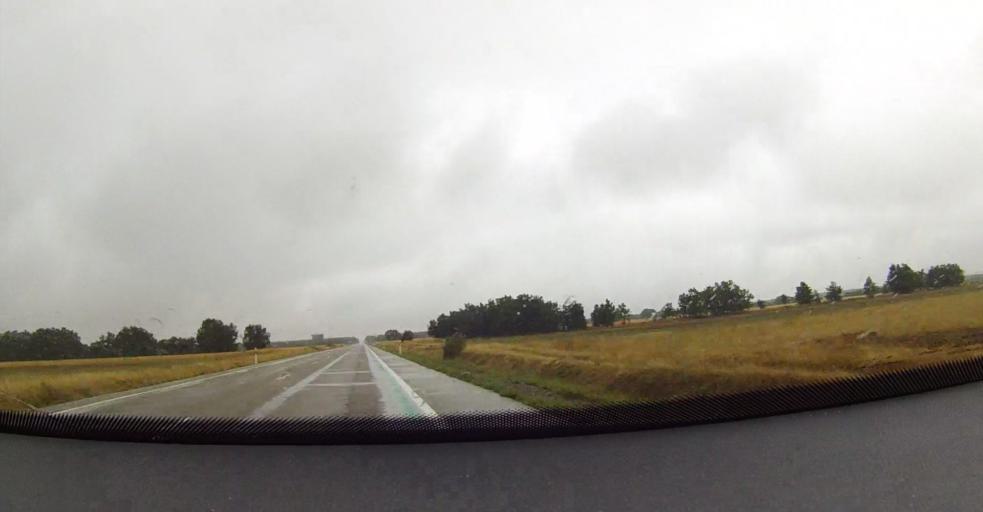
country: ES
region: Castille and Leon
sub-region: Provincia de Palencia
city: Pino del Rio
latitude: 42.6256
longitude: -4.7724
